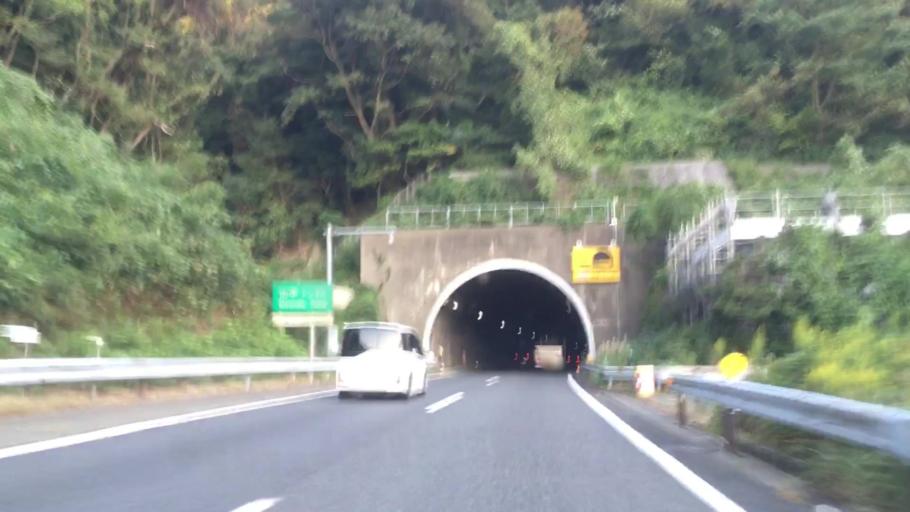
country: JP
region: Yamaguchi
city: Shimonoseki
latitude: 33.9507
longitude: 130.9905
